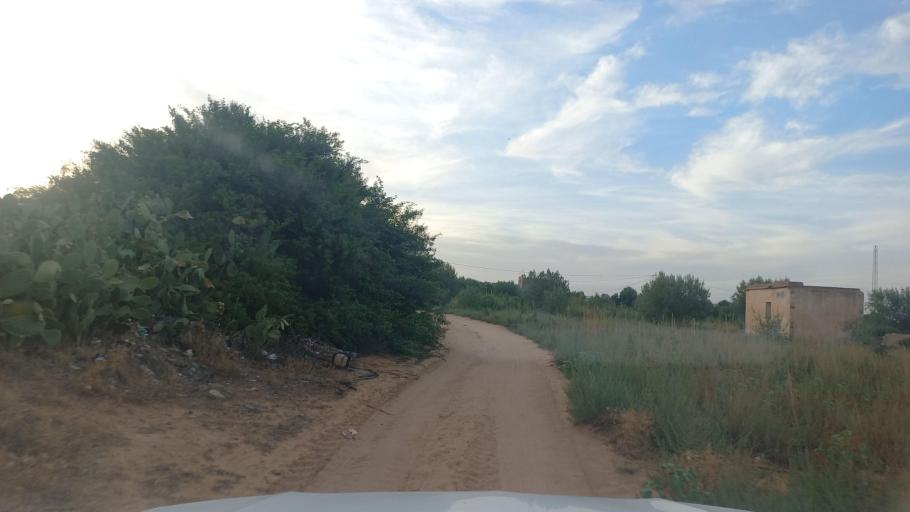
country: TN
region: Al Qasrayn
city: Kasserine
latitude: 35.2509
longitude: 9.0403
